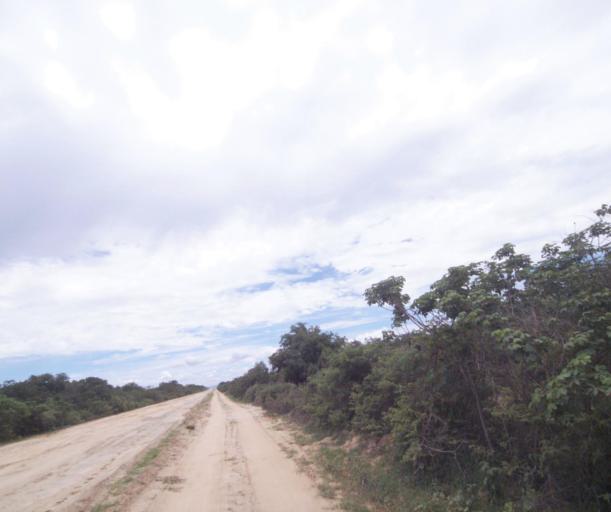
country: BR
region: Bahia
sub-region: Carinhanha
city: Carinhanha
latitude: -14.2631
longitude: -43.8186
